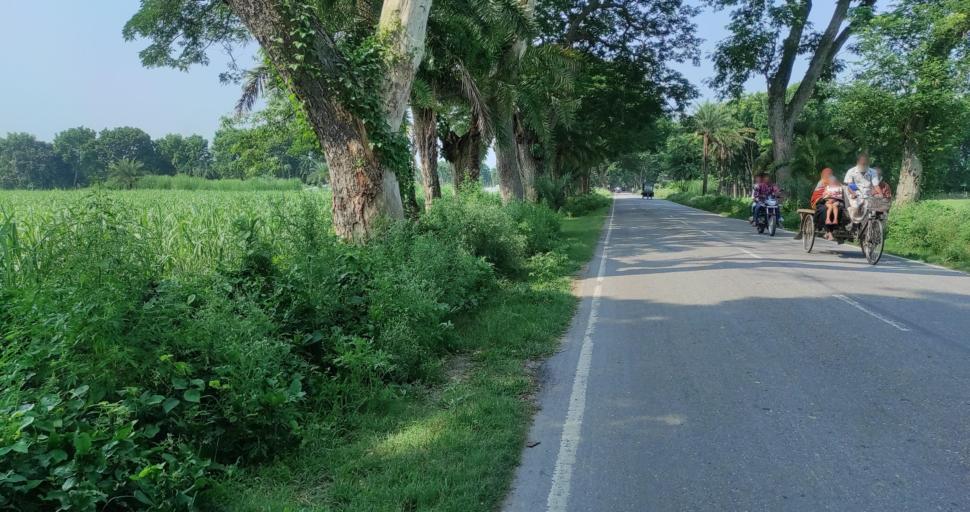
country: BD
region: Rajshahi
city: Ishurdi
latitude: 24.2778
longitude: 89.0585
